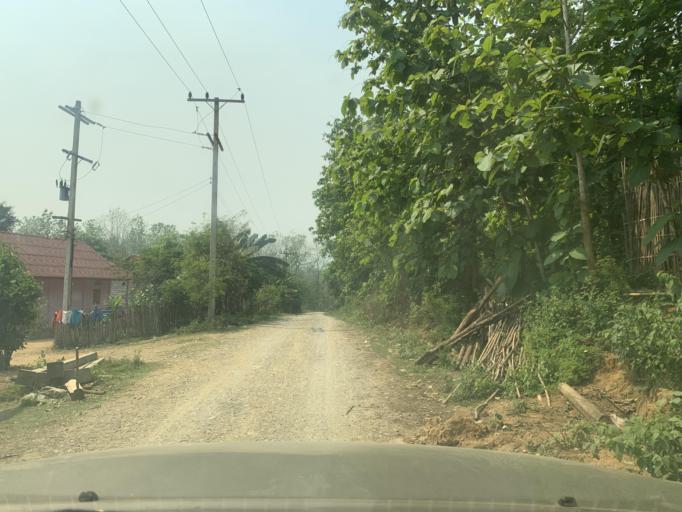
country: LA
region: Louangphabang
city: Louangphabang
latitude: 19.8844
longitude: 102.2532
